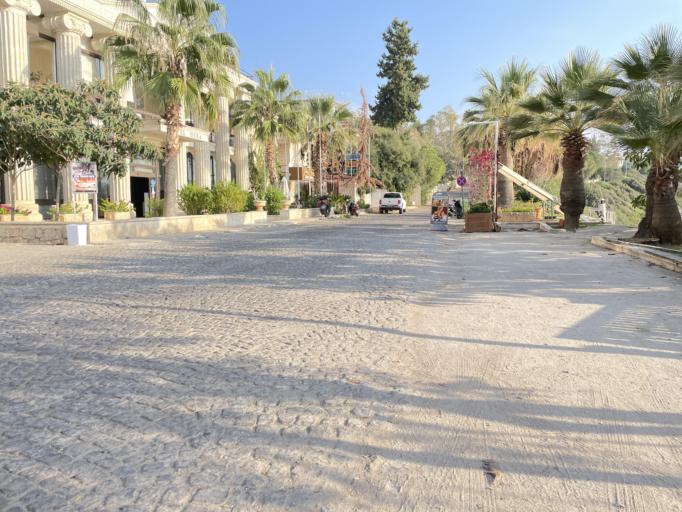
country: TR
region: Antalya
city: Kas
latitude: 36.1965
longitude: 29.6456
